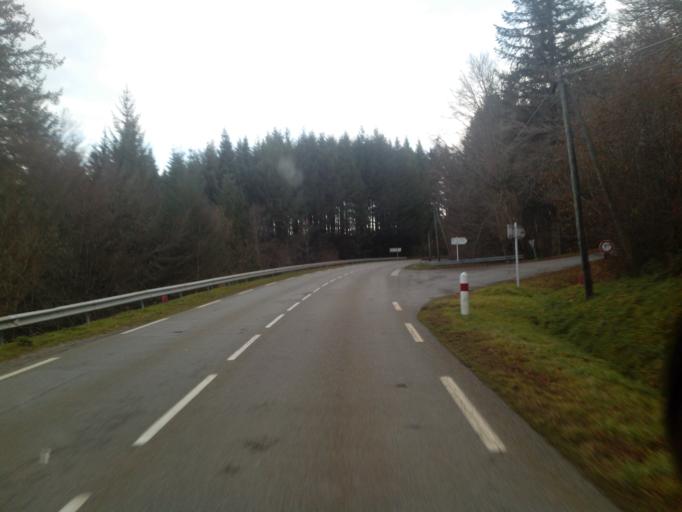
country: FR
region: Limousin
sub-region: Departement de la Correze
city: Meymac
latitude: 45.5767
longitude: 2.1360
